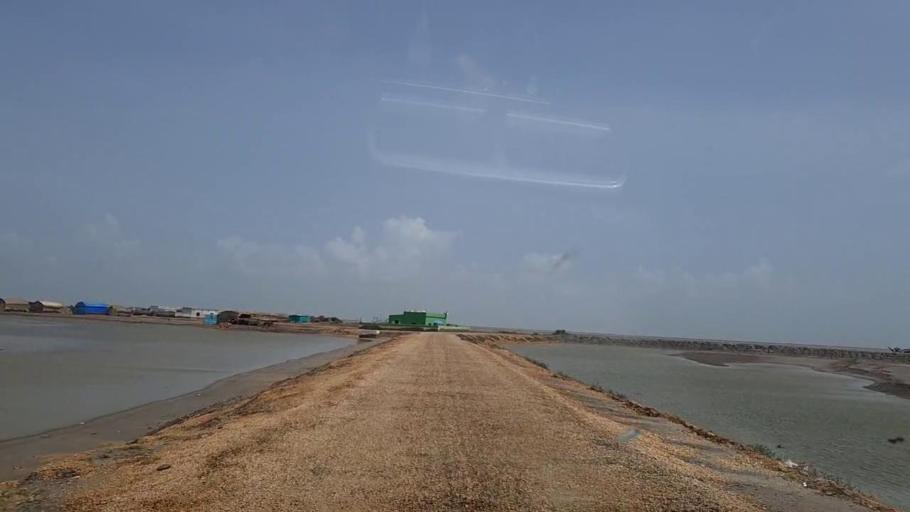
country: PK
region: Sindh
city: Keti Bandar
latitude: 24.1289
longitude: 67.4626
